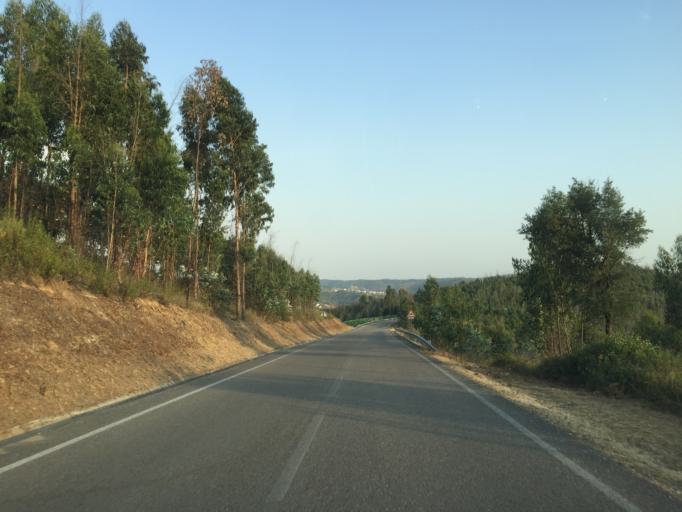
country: PT
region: Santarem
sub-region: Ferreira do Zezere
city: Ferreira do Zezere
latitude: 39.5861
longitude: -8.2974
